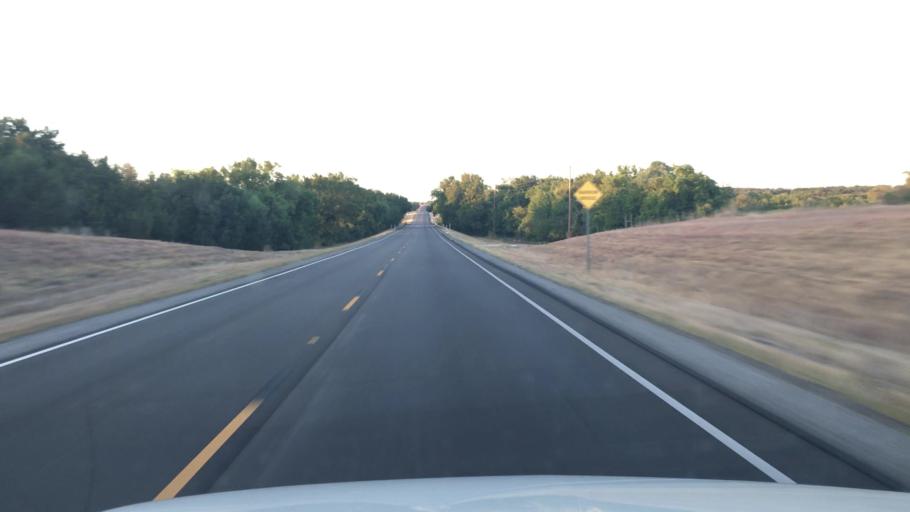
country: US
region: Texas
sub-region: Hamilton County
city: Hico
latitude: 32.0440
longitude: -98.0045
